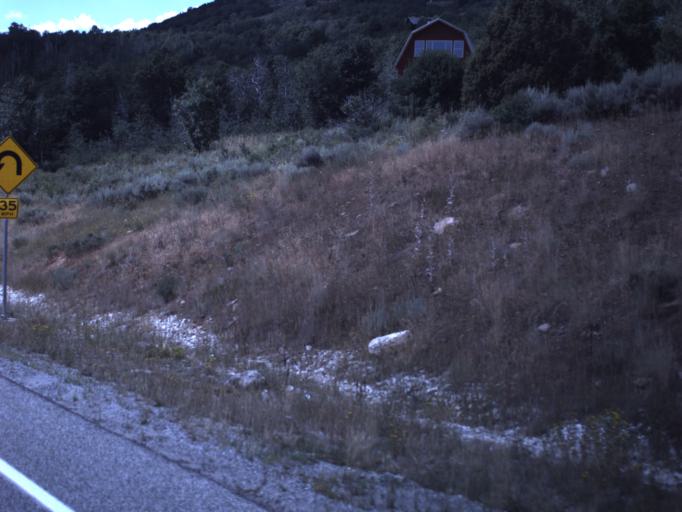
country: US
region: Idaho
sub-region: Bear Lake County
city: Paris
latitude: 41.9245
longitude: -111.4298
